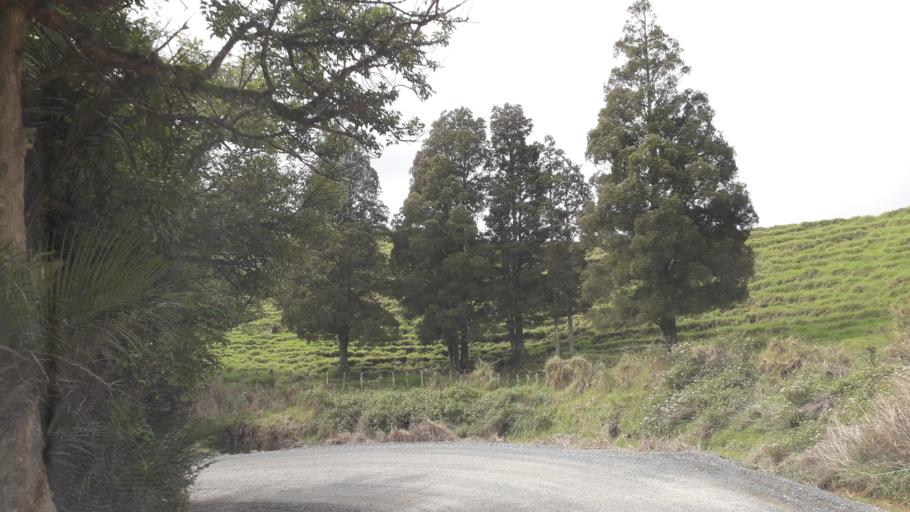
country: NZ
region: Northland
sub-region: Far North District
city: Kaitaia
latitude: -35.1918
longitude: 173.2894
